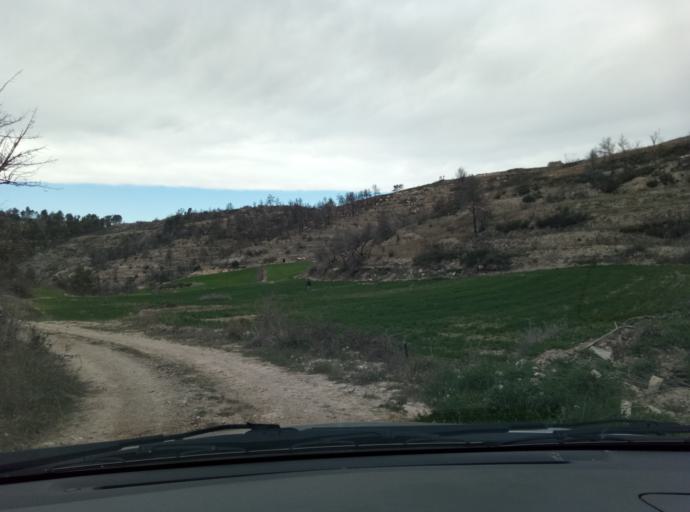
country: ES
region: Catalonia
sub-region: Provincia de Lleida
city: Nalec
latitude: 41.5172
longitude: 1.1354
